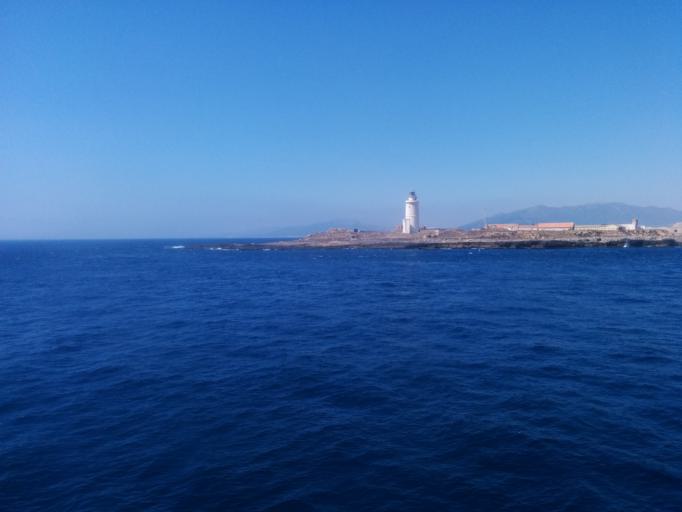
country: ES
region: Andalusia
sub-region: Provincia de Cadiz
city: Tarifa
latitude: 35.9982
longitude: -5.6063
